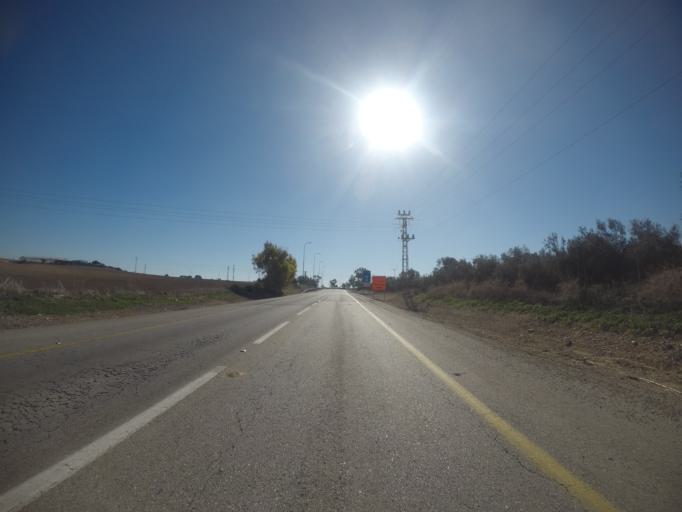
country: IL
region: Southern District
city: Ashqelon
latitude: 31.6853
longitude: 34.6520
